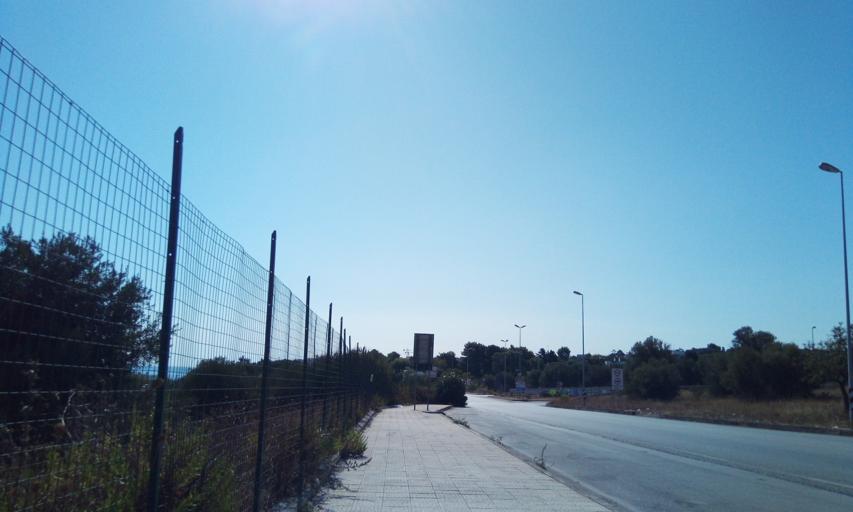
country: IT
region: Apulia
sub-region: Provincia di Bari
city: Polignano a Mare
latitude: 41.0042
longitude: 17.1989
